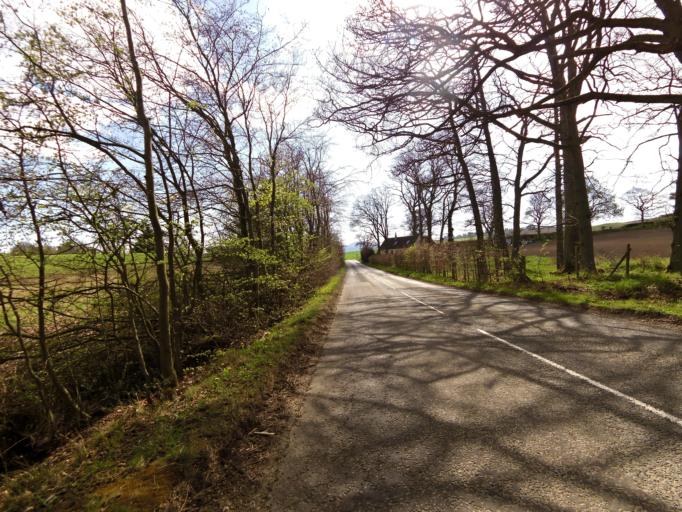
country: GB
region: Scotland
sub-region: Fife
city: Auchtermuchty
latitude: 56.3141
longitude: -3.2343
